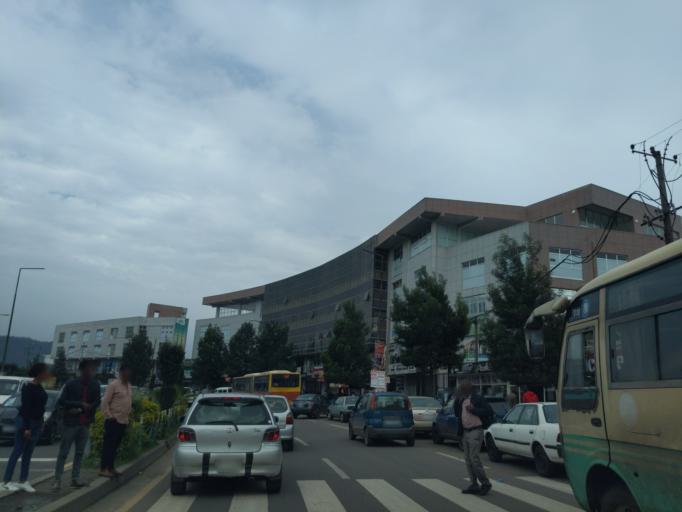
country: ET
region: Adis Abeba
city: Addis Ababa
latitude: 9.0322
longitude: 38.7650
